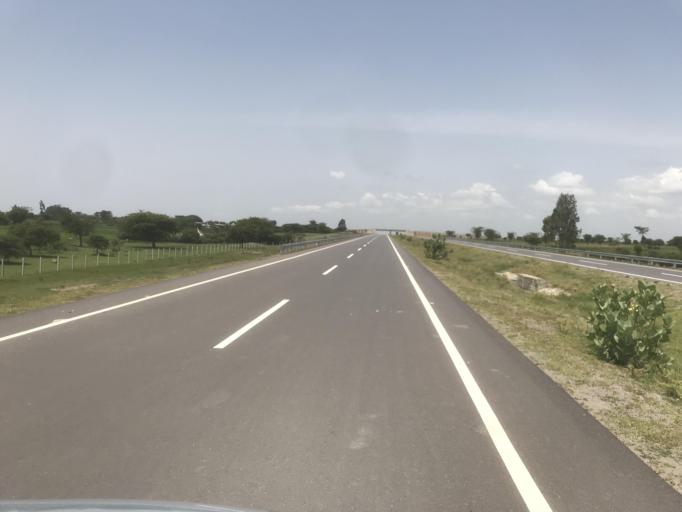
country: ET
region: Oromiya
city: Ziway
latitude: 8.2564
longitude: 38.8953
